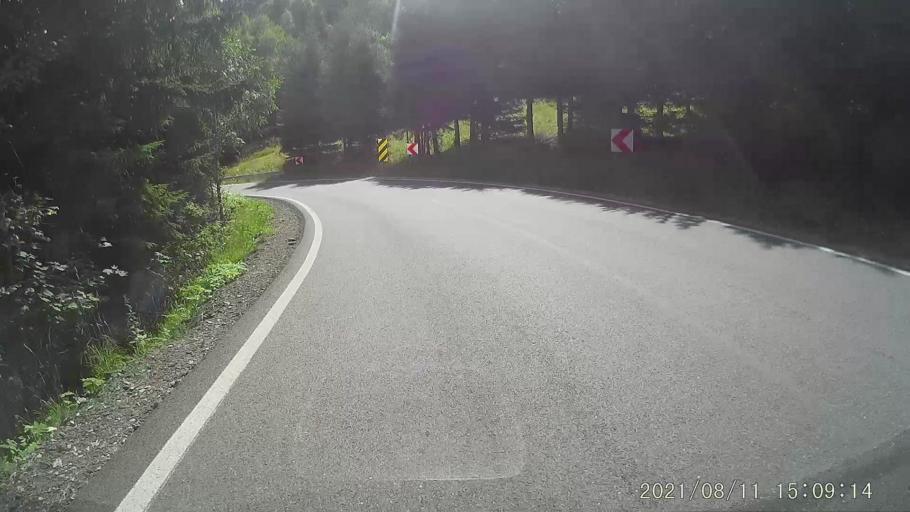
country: PL
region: Lower Silesian Voivodeship
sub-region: Powiat klodzki
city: Stronie Slaskie
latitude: 50.2614
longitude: 16.8131
